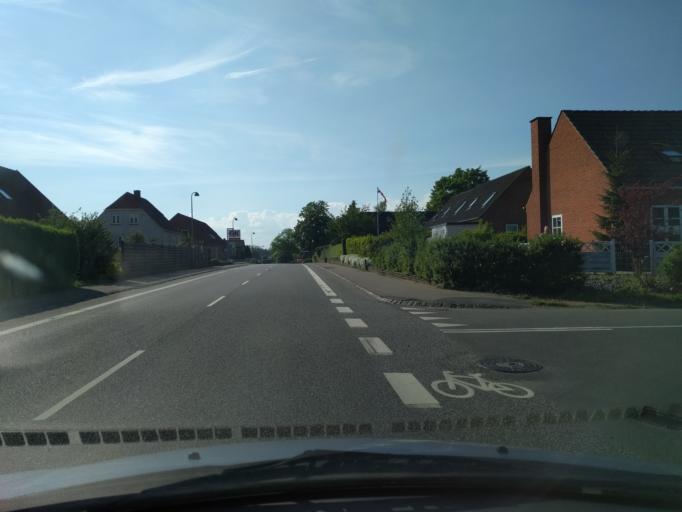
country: DK
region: Zealand
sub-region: Slagelse Kommune
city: Skaelskor
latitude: 55.3033
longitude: 11.2703
